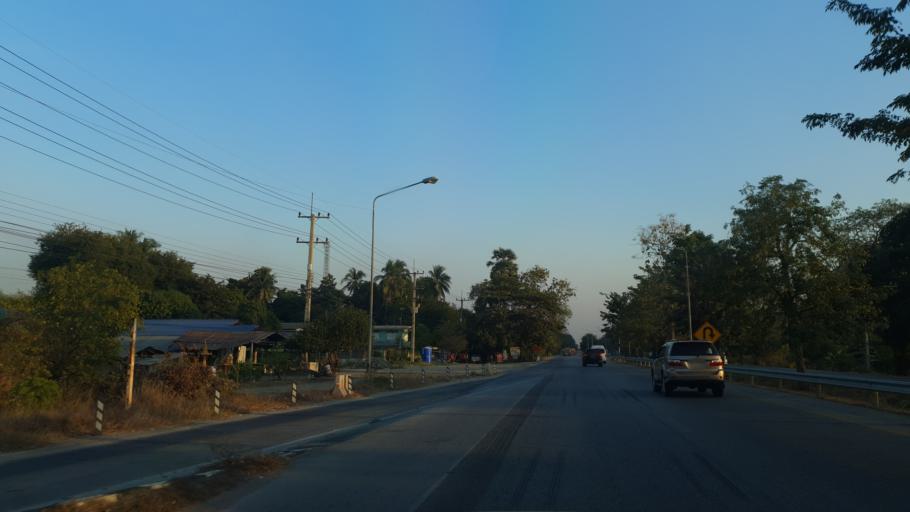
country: TH
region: Nakhon Sawan
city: Banphot Phisai
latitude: 15.9175
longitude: 99.8819
